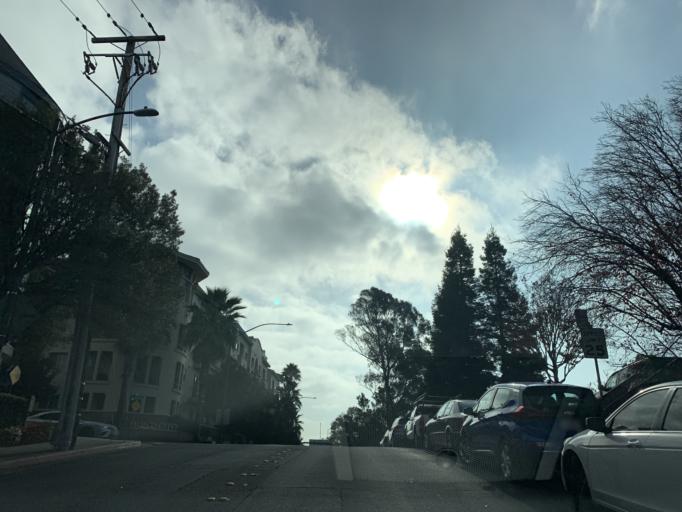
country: US
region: California
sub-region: Contra Costa County
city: Walnut Creek
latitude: 37.8945
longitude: -122.0655
